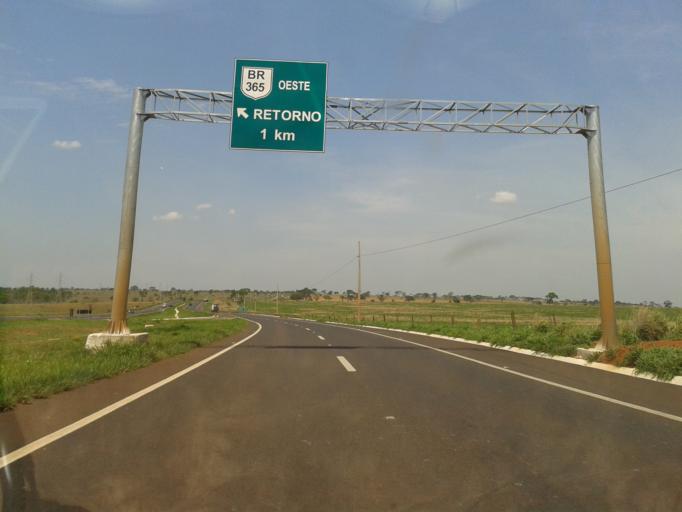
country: BR
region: Minas Gerais
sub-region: Monte Alegre De Minas
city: Monte Alegre de Minas
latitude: -18.8497
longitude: -48.8263
